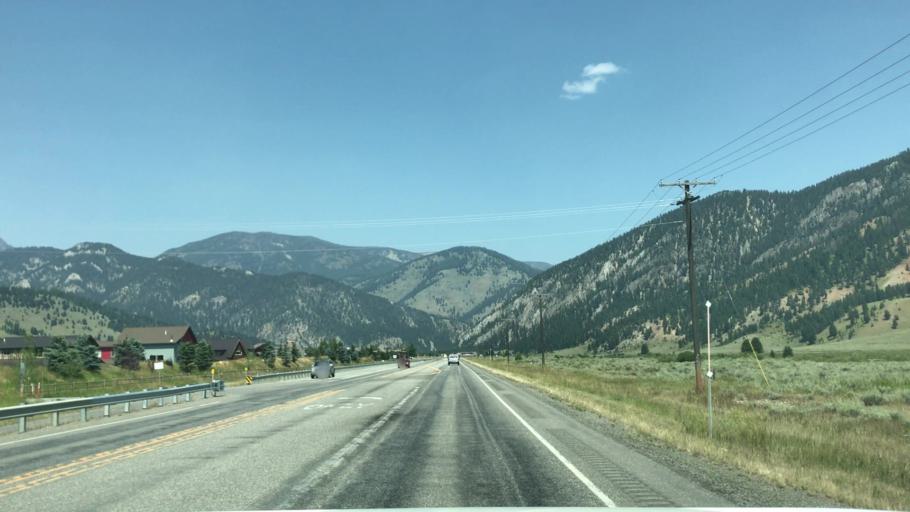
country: US
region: Montana
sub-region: Gallatin County
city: Big Sky
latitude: 45.2390
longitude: -111.2508
